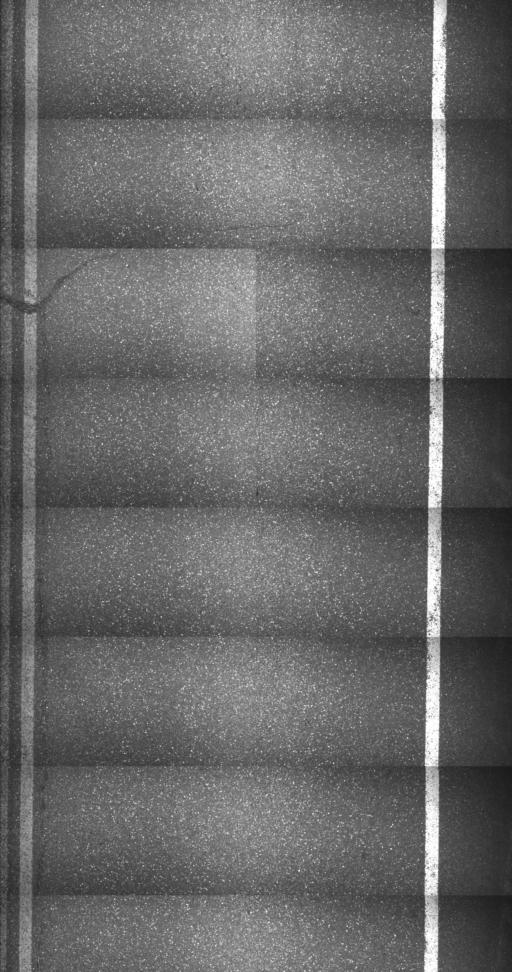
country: US
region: Vermont
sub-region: Washington County
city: Northfield
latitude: 44.1235
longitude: -72.6566
